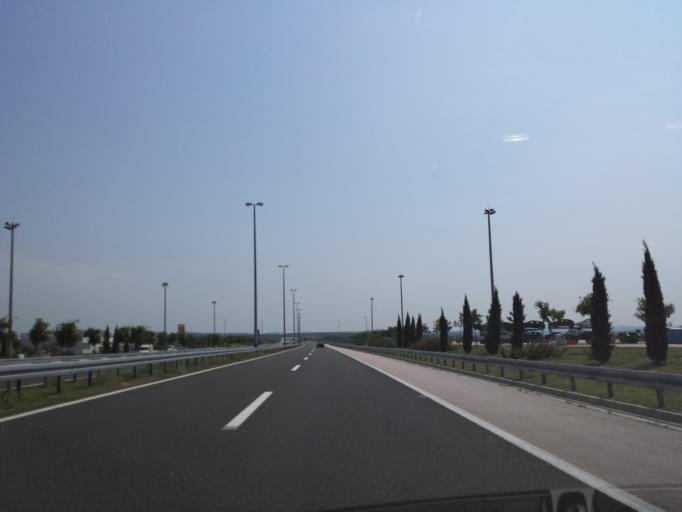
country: HR
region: Zadarska
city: Polaca
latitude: 44.0622
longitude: 15.5301
